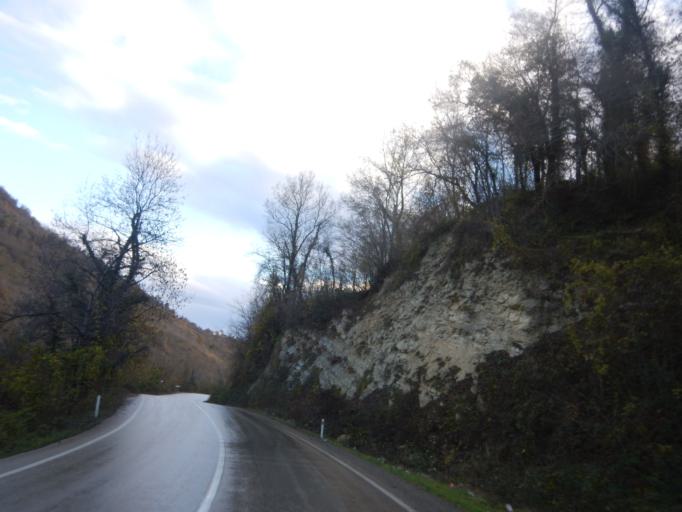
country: TR
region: Ordu
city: Kumru
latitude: 40.9020
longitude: 37.3206
